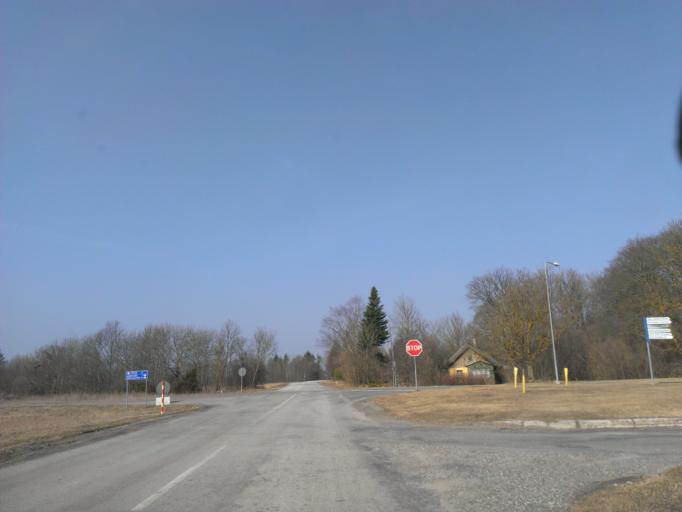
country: EE
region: Saare
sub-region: Orissaare vald
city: Orissaare
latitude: 58.5037
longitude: 23.1135
